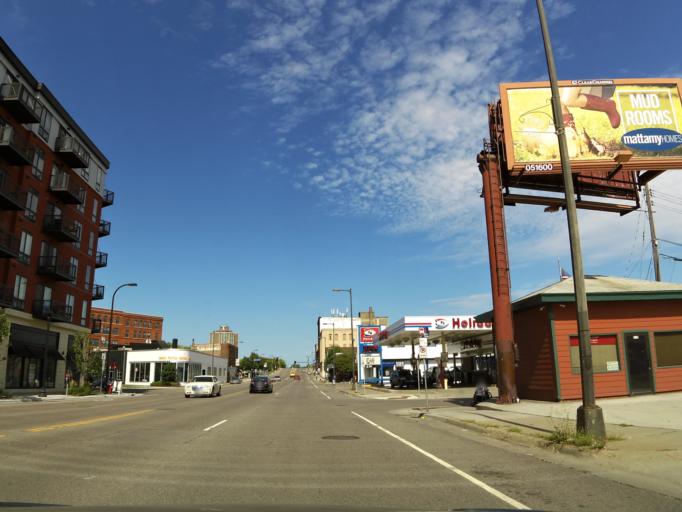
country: US
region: Minnesota
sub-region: Hennepin County
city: Minneapolis
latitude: 44.9894
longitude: -93.2527
